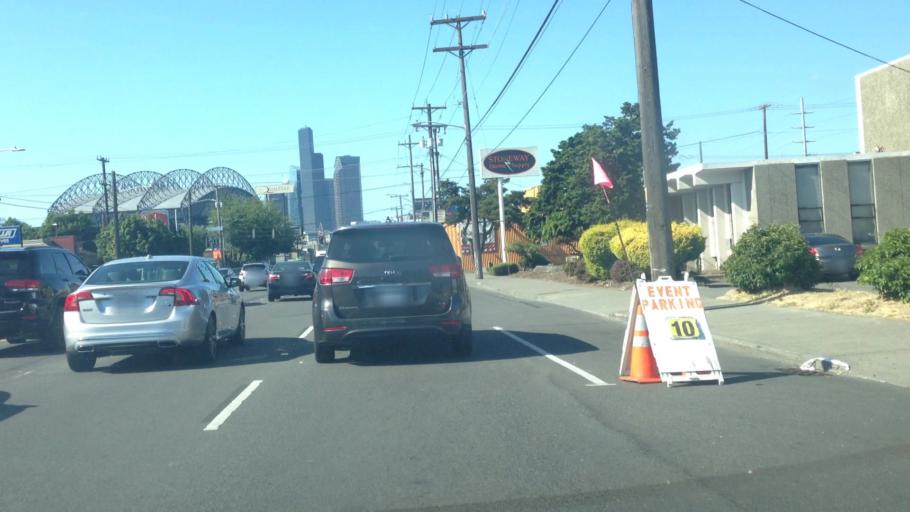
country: US
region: Washington
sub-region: King County
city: Seattle
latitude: 47.5849
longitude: -122.3289
